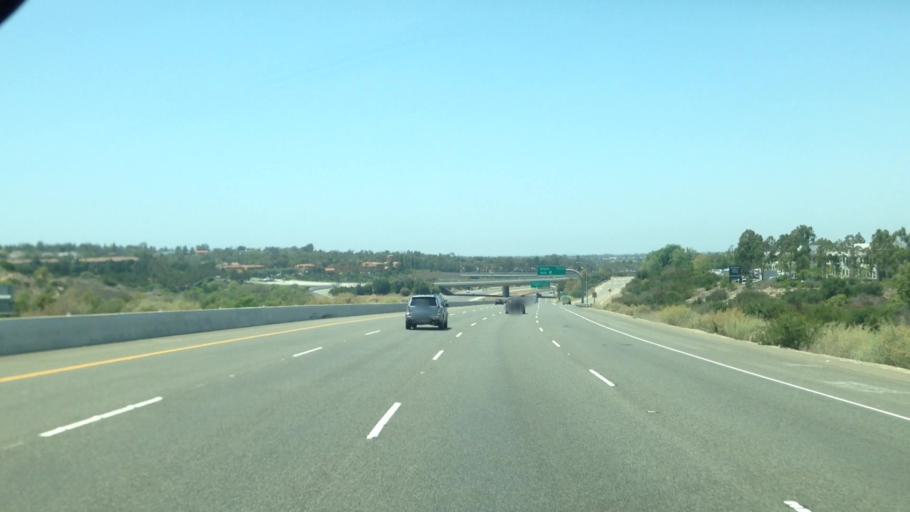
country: US
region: California
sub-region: Orange County
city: San Joaquin Hills
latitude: 33.6341
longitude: -117.8507
